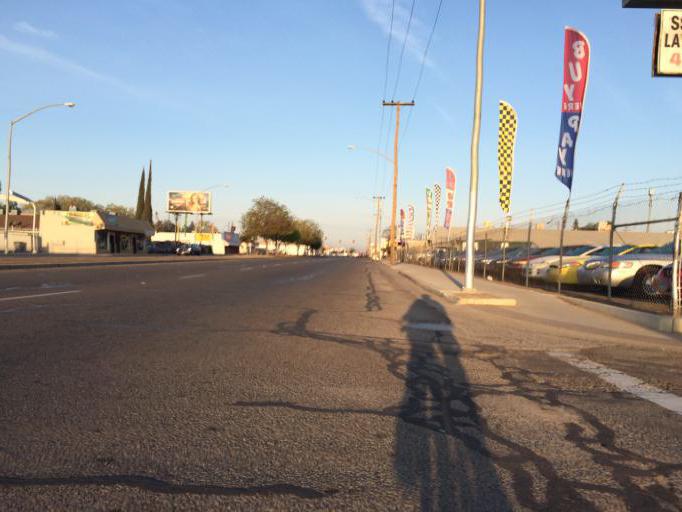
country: US
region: California
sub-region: Fresno County
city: Fresno
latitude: 36.7506
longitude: -119.7432
